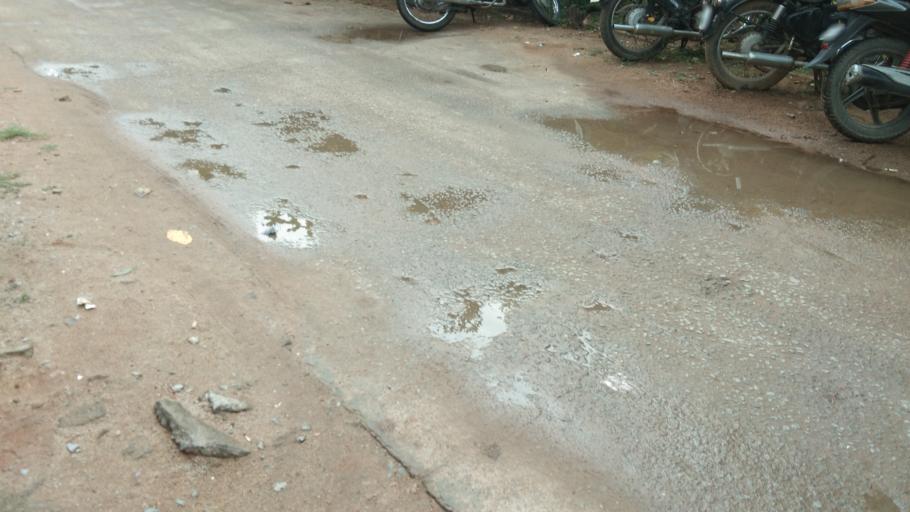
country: IN
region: Telangana
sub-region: Hyderabad
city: Malkajgiri
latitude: 17.4608
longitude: 78.5391
